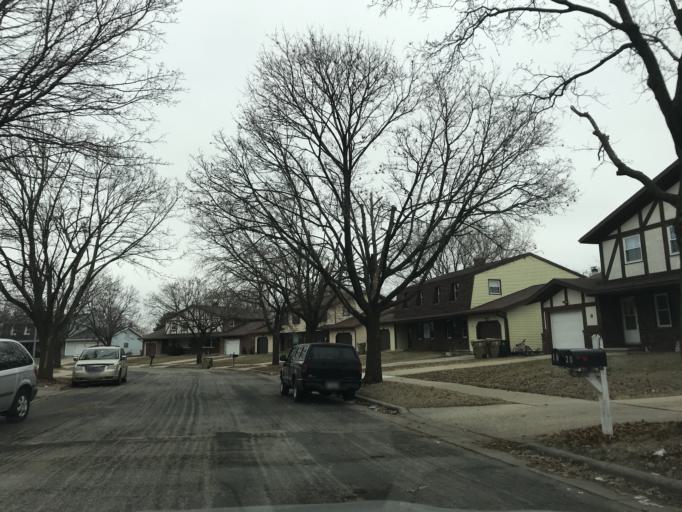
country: US
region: Wisconsin
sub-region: Dane County
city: Monona
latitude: 43.0998
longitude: -89.2873
